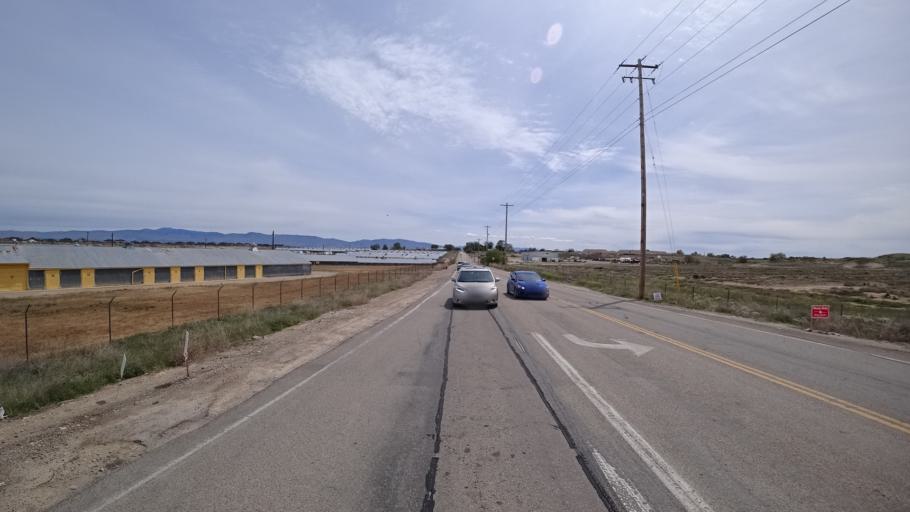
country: US
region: Idaho
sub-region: Ada County
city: Meridian
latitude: 43.5610
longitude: -116.3934
